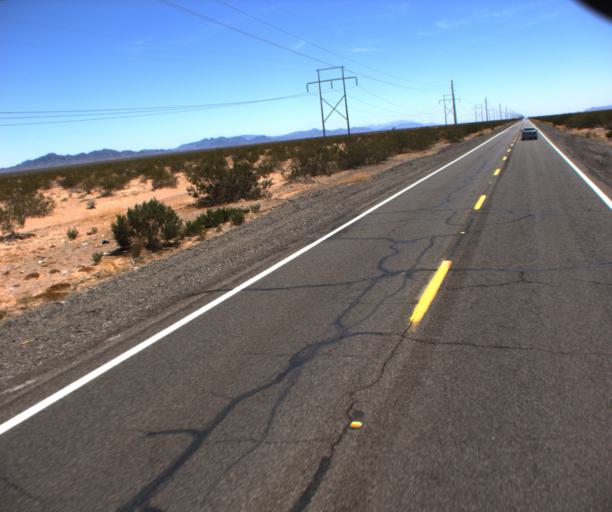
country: US
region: Arizona
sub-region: La Paz County
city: Parker
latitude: 33.9397
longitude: -114.2169
